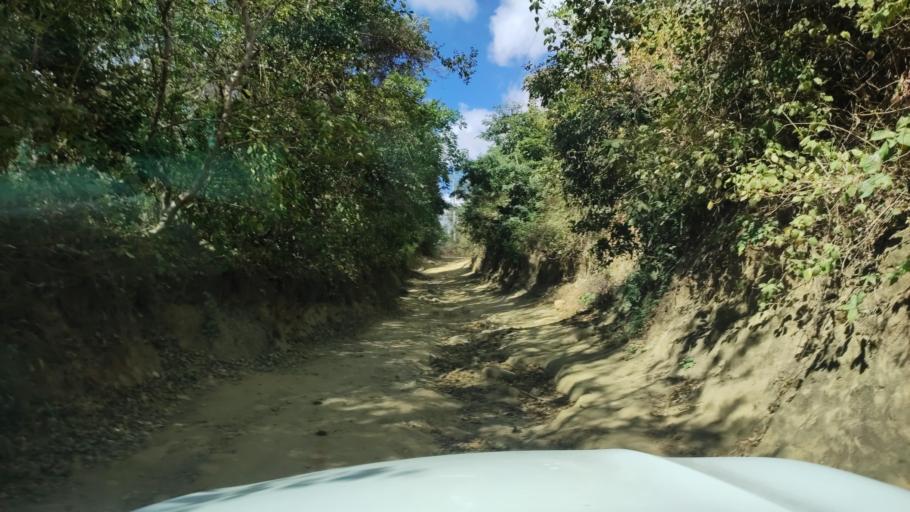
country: NI
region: Carazo
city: Santa Teresa
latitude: 11.6550
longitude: -86.1854
